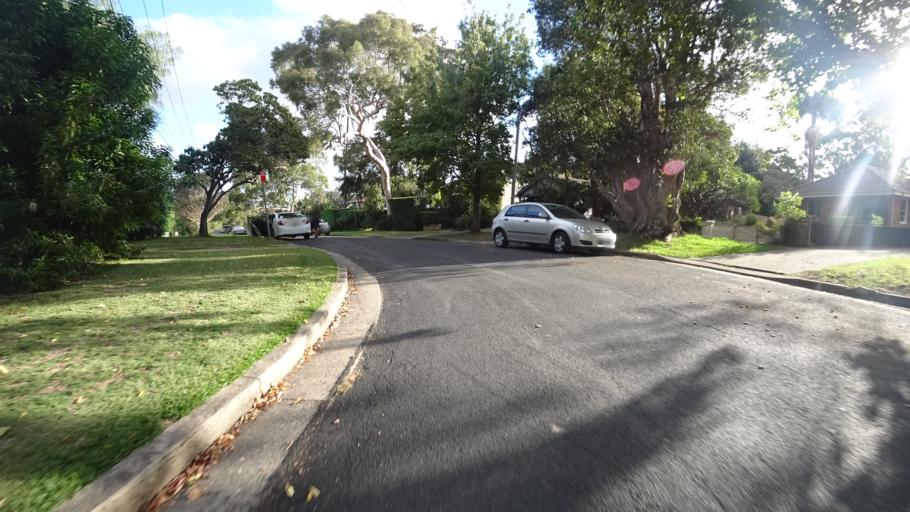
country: AU
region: New South Wales
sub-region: Lane Cove
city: Lane Cove West
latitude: -33.8159
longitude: 151.1535
